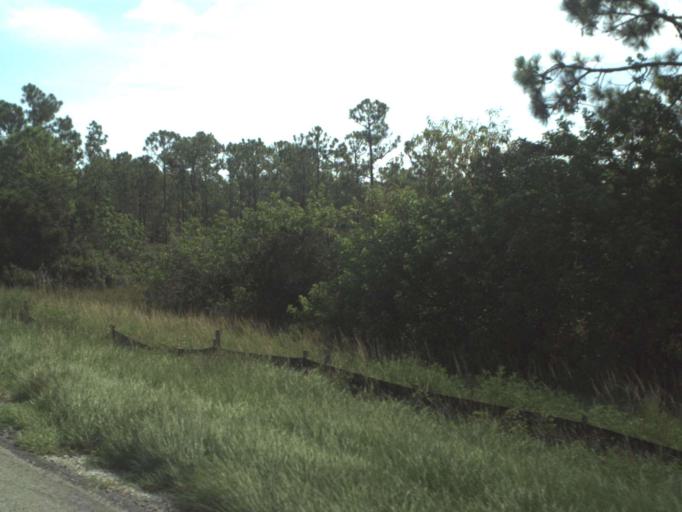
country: US
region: Florida
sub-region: Indian River County
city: Roseland
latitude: 27.8049
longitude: -80.5486
